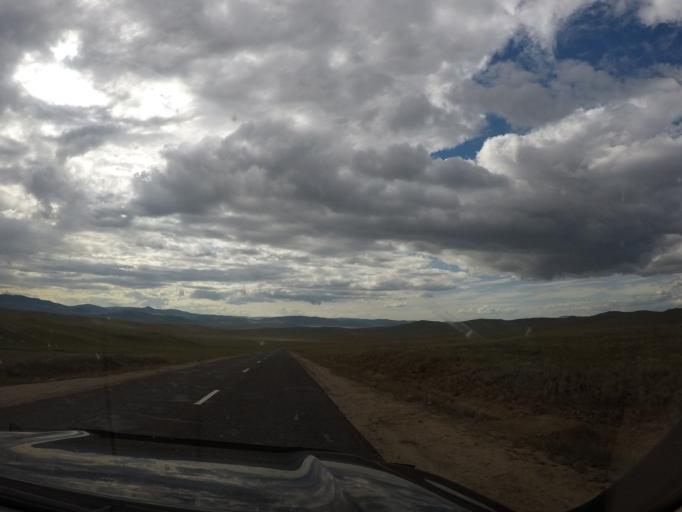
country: MN
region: Hentiy
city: Modot
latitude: 47.5899
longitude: 109.2735
